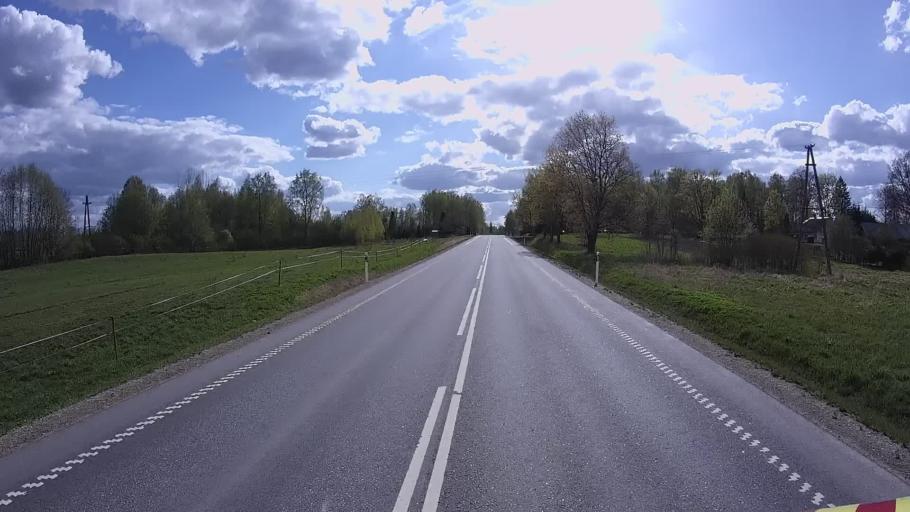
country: EE
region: Jogevamaa
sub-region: Mustvee linn
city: Mustvee
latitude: 58.8377
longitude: 26.8120
